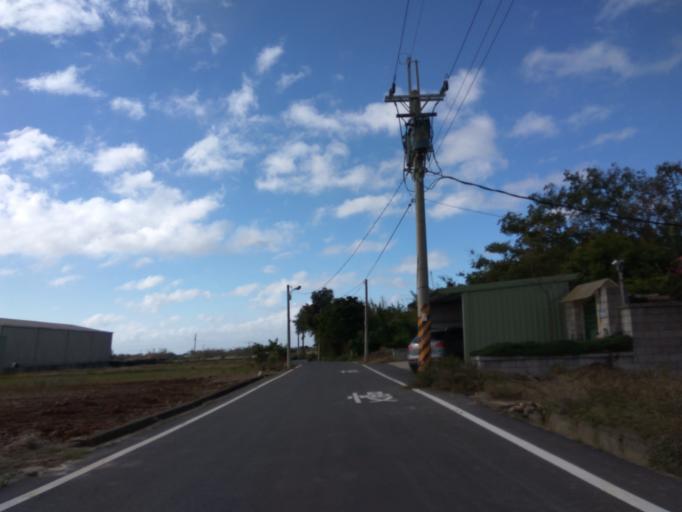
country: TW
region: Taiwan
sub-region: Hsinchu
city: Zhubei
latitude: 24.9739
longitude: 121.0730
